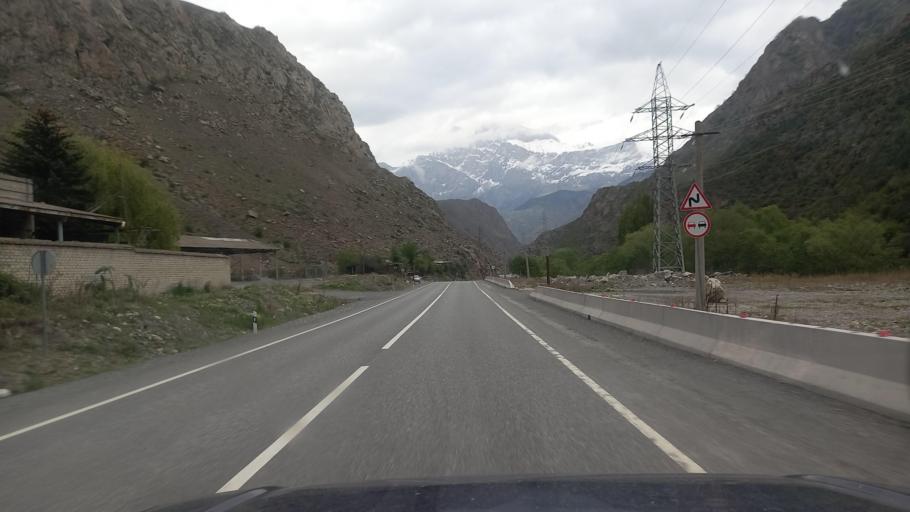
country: RU
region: North Ossetia
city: Mizur
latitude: 42.8552
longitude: 44.0938
